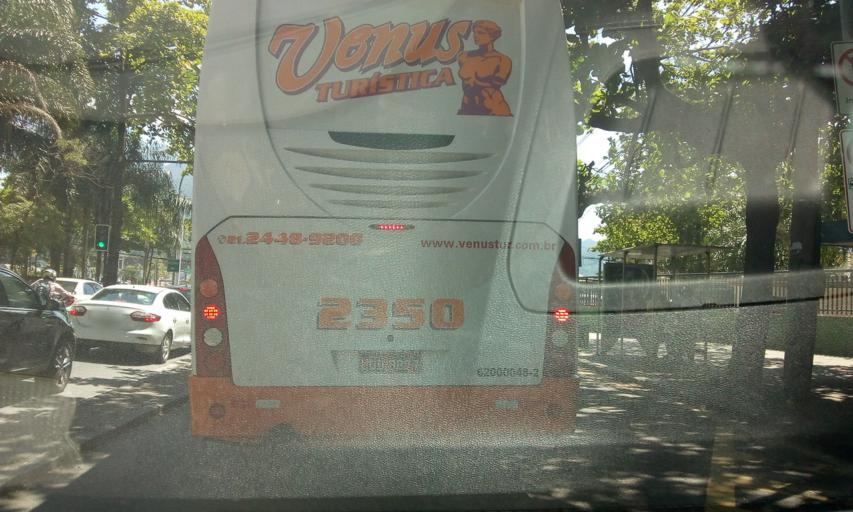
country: BR
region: Rio de Janeiro
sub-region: Rio De Janeiro
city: Rio de Janeiro
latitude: -23.0043
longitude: -43.3254
